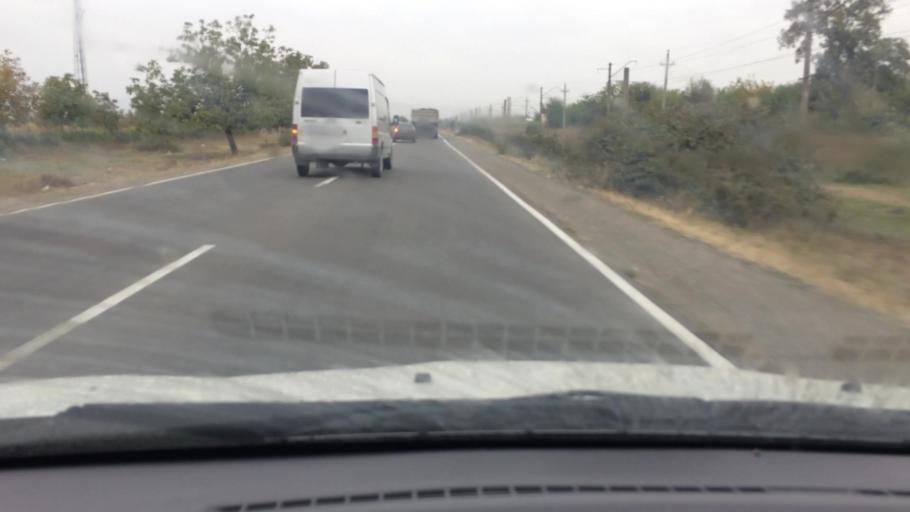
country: GE
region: Kvemo Kartli
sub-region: Marneuli
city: Marneuli
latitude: 41.4323
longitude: 44.8207
